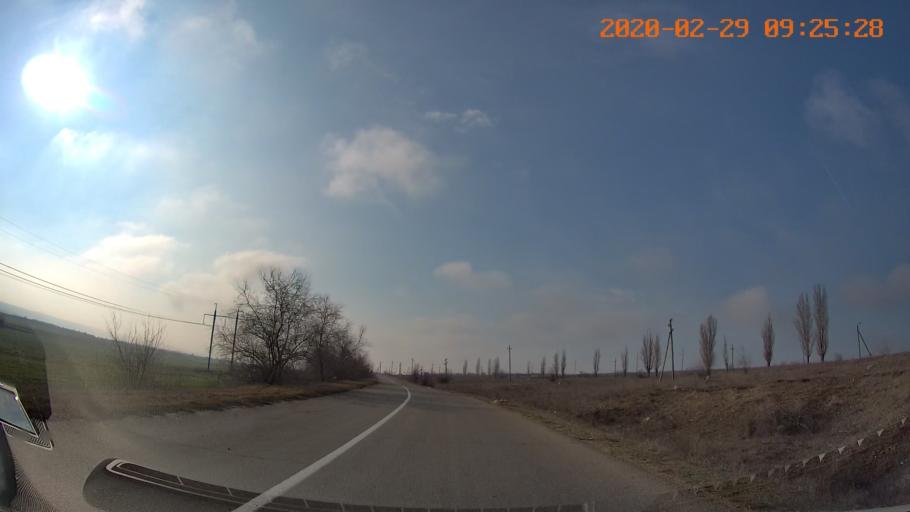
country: MD
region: Telenesti
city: Pervomaisc
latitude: 46.7082
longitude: 29.9526
